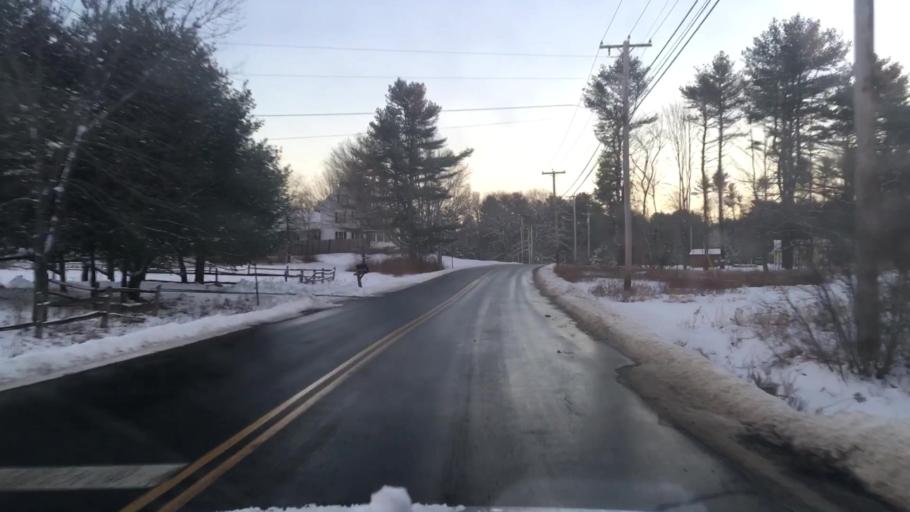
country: US
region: Maine
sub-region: Sagadahoc County
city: Topsham
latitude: 43.9582
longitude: -69.9286
